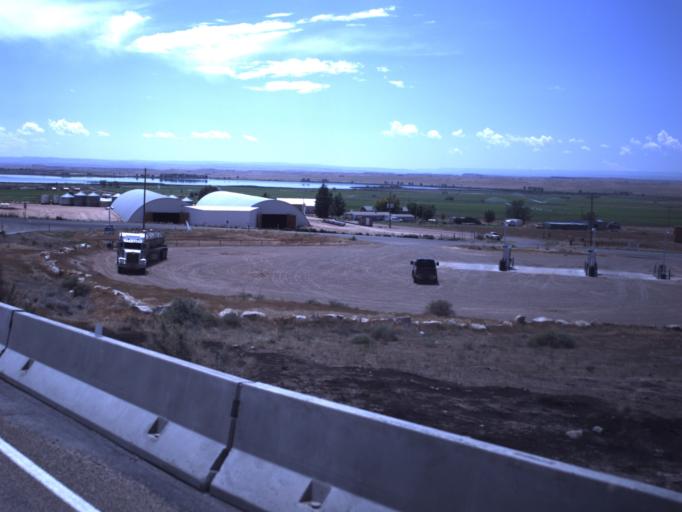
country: US
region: Utah
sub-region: Uintah County
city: Maeser
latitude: 40.2214
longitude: -109.6830
